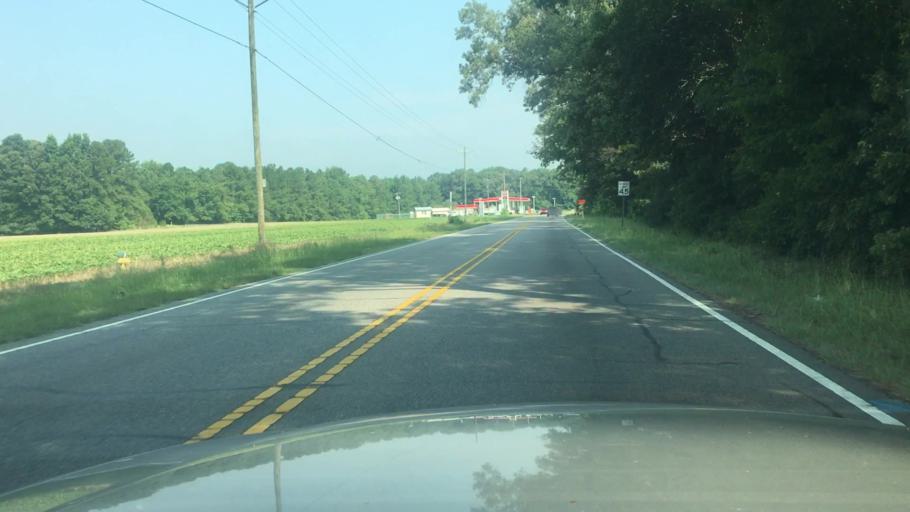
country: US
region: North Carolina
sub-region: Cumberland County
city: Hope Mills
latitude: 34.9329
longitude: -78.9182
